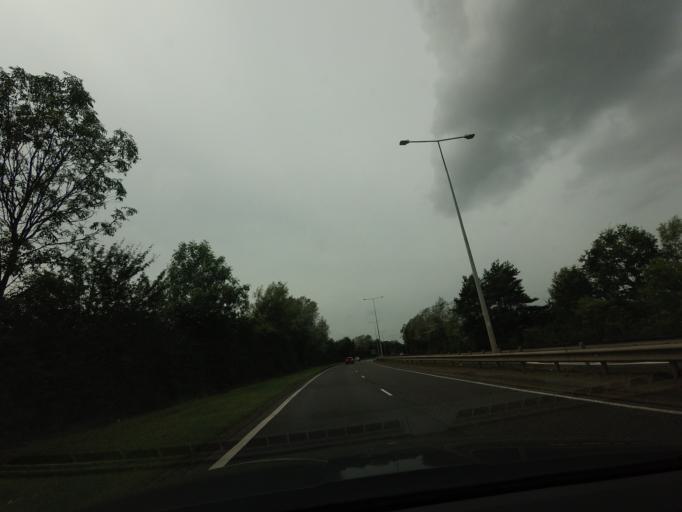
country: GB
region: England
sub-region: Telford and Wrekin
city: Telford
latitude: 52.6697
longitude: -2.4209
